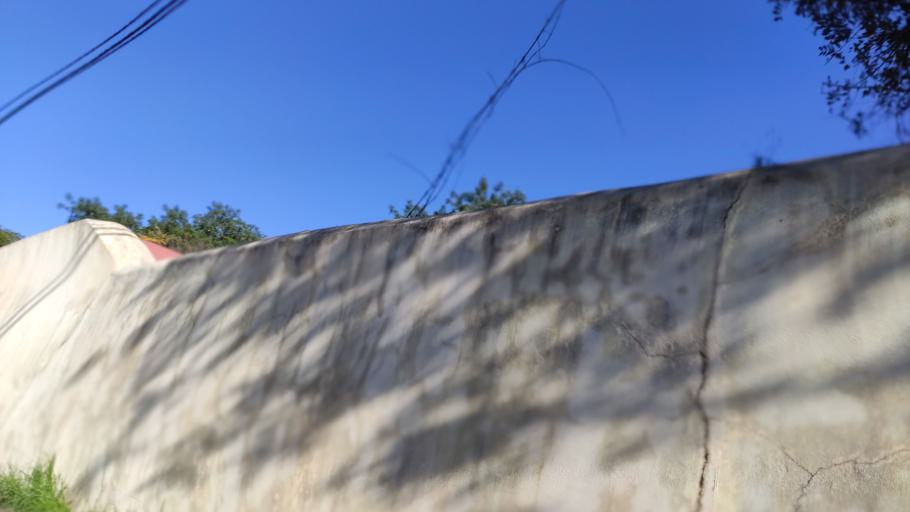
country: PT
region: Faro
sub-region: Sao Bras de Alportel
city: Sao Bras de Alportel
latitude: 37.1546
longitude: -7.9080
